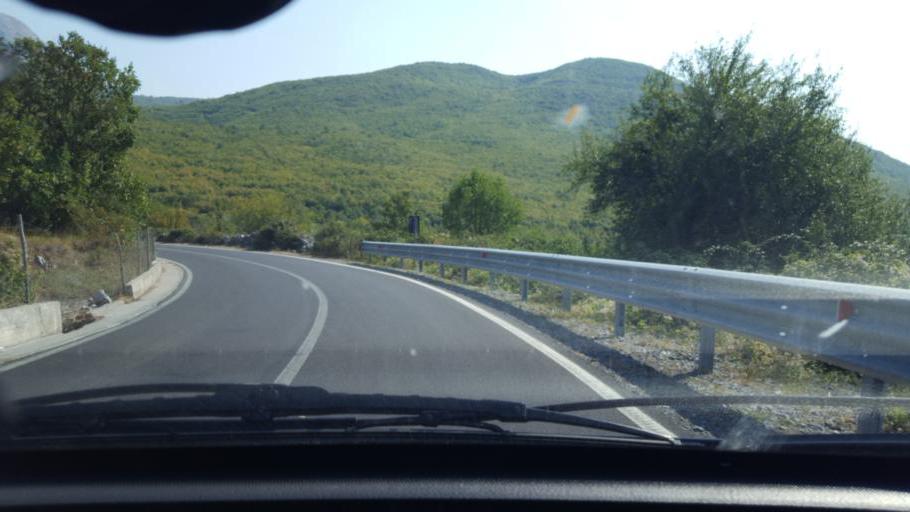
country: AL
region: Shkoder
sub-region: Rrethi i Malesia e Madhe
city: Kastrat
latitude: 42.3848
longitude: 19.4919
